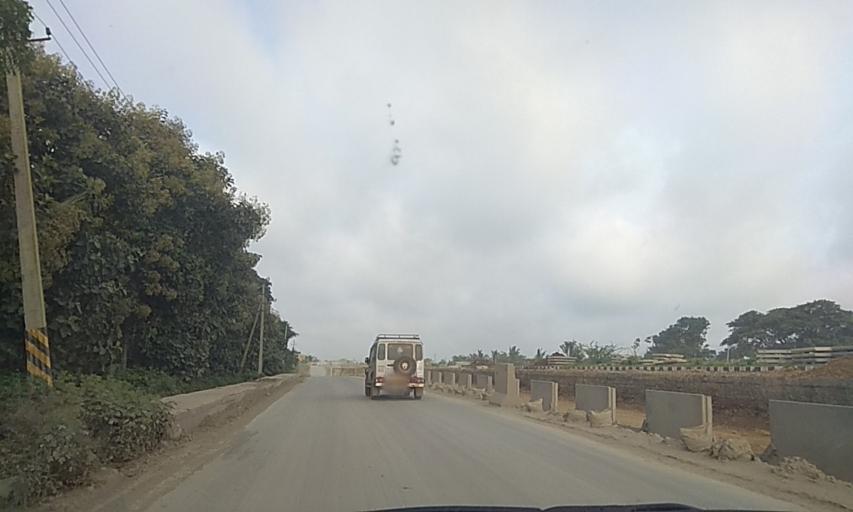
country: IN
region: Karnataka
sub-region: Haveri
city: Haveri
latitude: 14.7733
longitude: 75.4186
